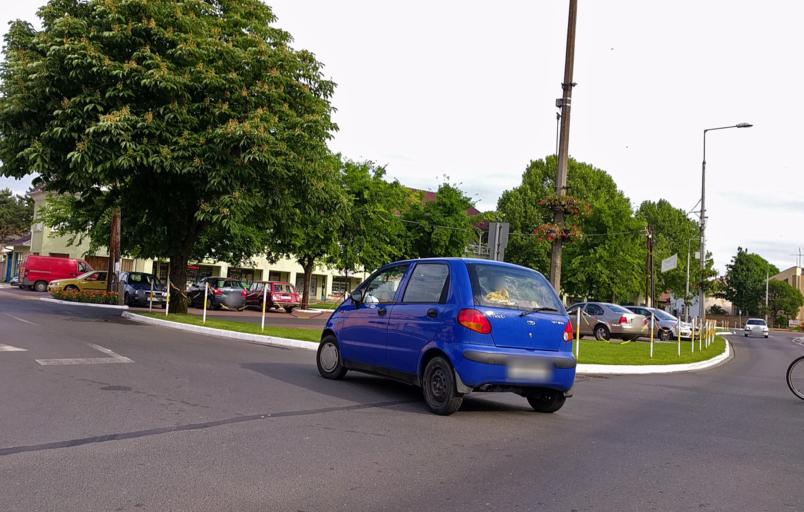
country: HU
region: Bacs-Kiskun
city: Tiszakecske
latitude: 46.9321
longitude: 20.0955
